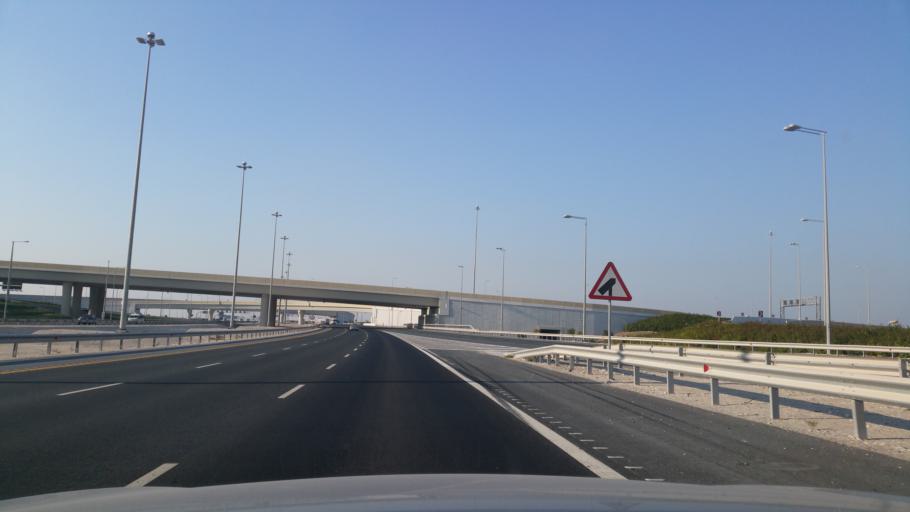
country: QA
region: Al Wakrah
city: Al Wakrah
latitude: 25.1302
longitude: 51.5870
